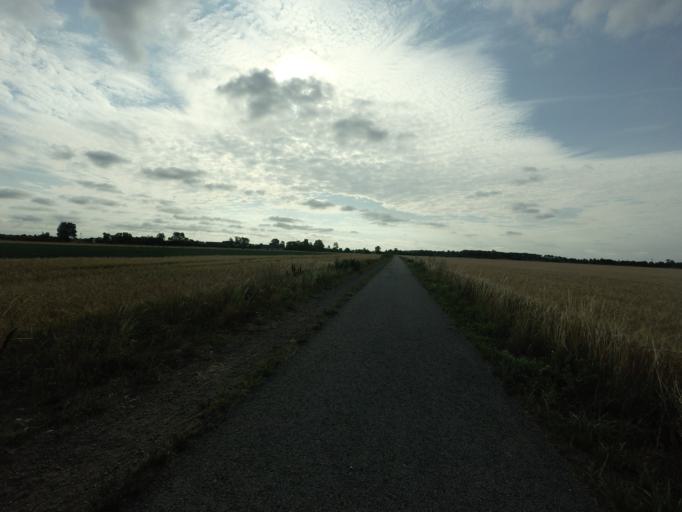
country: SE
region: Skane
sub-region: Hoganas Kommun
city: Hoganas
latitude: 56.1846
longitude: 12.6426
